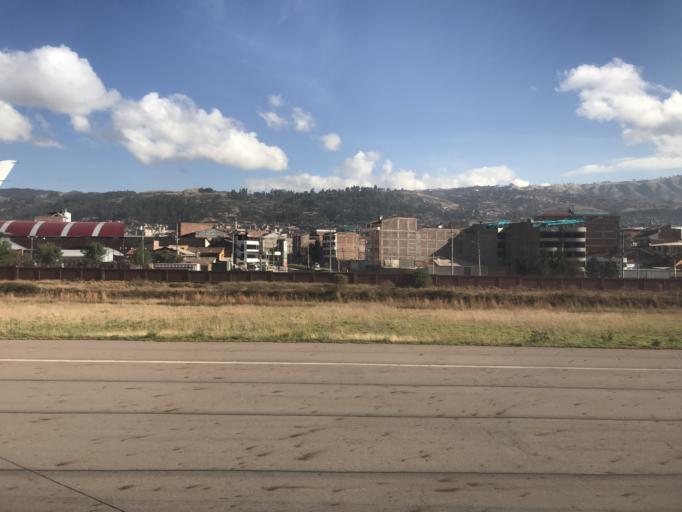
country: PE
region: Cusco
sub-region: Provincia de Cusco
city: Cusco
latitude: -13.5357
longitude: -71.9394
